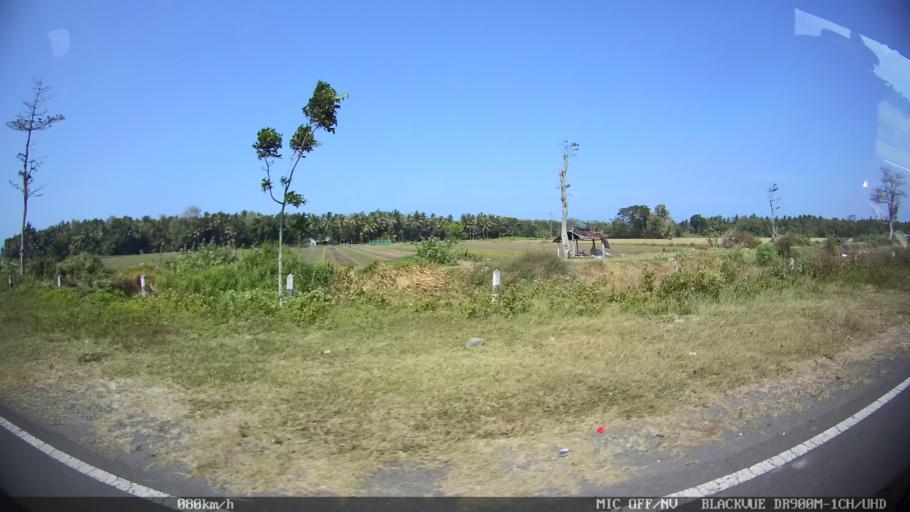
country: ID
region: Daerah Istimewa Yogyakarta
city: Srandakan
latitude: -7.9575
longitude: 110.2004
